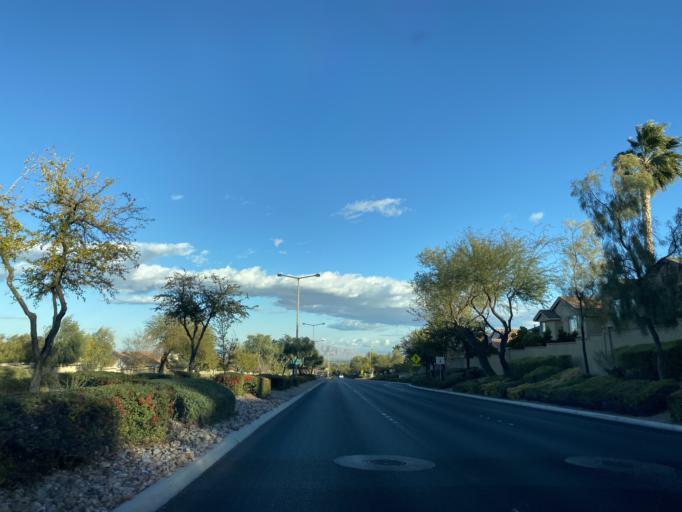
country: US
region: Nevada
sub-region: Clark County
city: Summerlin South
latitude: 36.2048
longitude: -115.3169
